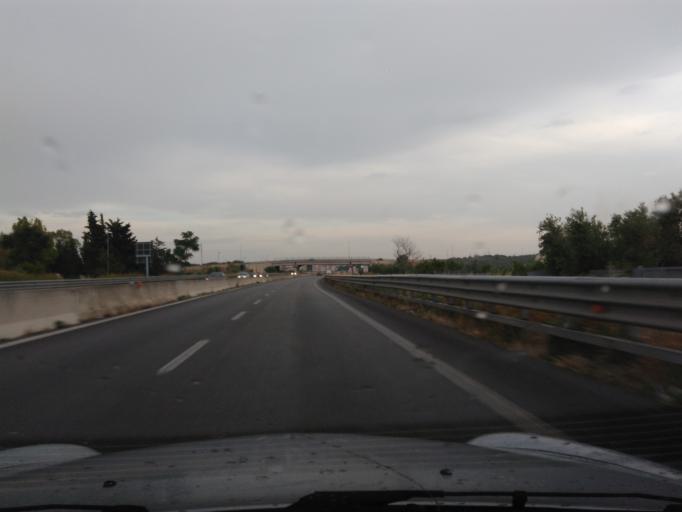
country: IT
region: Apulia
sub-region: Provincia di Bari
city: Molfetta
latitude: 41.1975
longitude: 16.5785
